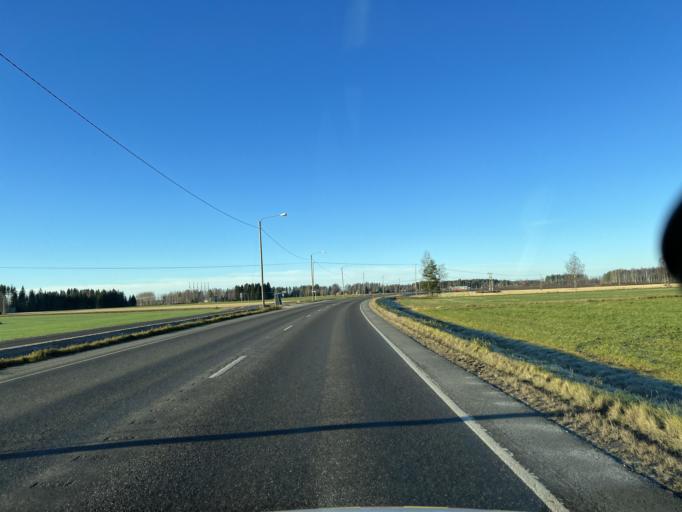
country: FI
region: Northern Ostrobothnia
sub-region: Nivala-Haapajaervi
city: Nivala
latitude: 63.9511
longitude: 24.8831
